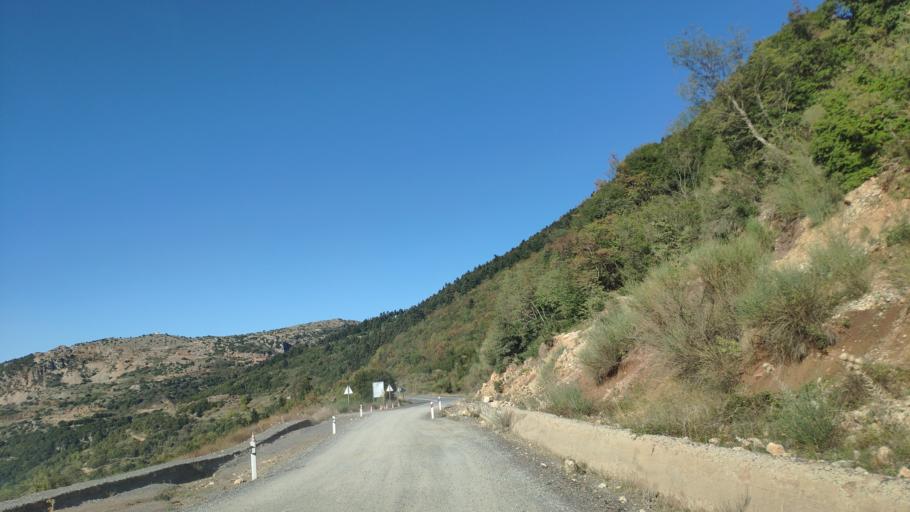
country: GR
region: Peloponnese
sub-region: Nomos Arkadias
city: Dimitsana
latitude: 37.5679
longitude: 22.0604
